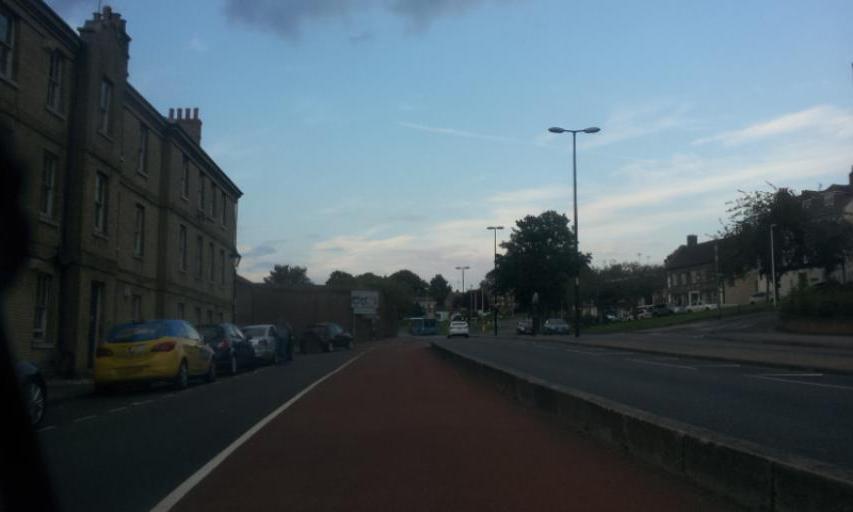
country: GB
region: England
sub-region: Kent
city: Chatham
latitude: 51.3921
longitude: 0.5272
